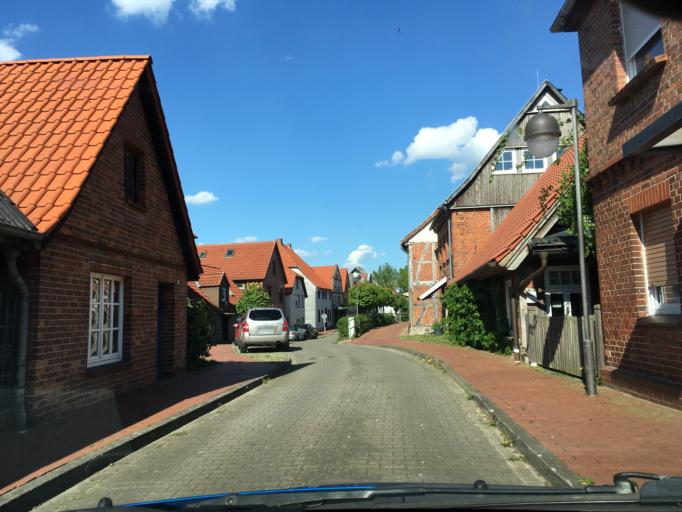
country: DE
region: Brandenburg
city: Lanz
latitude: 53.0355
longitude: 11.5644
